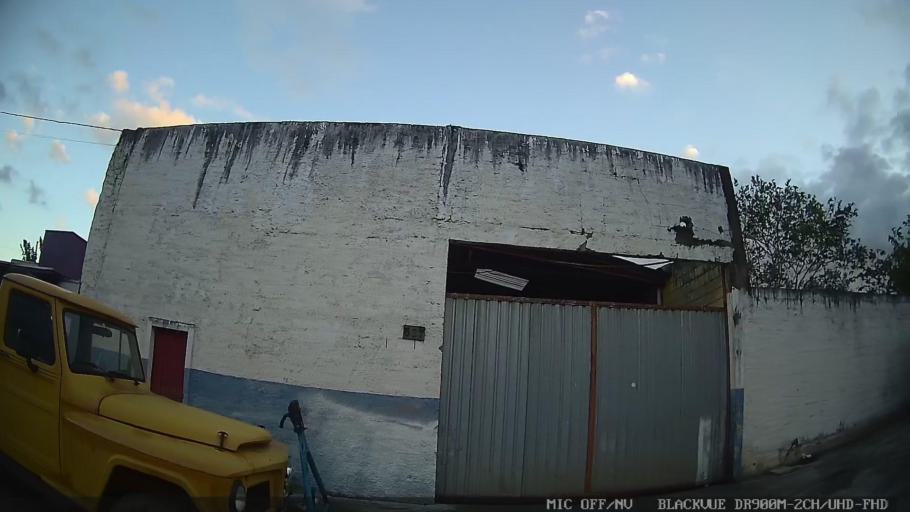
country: BR
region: Sao Paulo
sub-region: Caraguatatuba
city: Caraguatatuba
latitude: -23.6649
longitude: -45.4456
